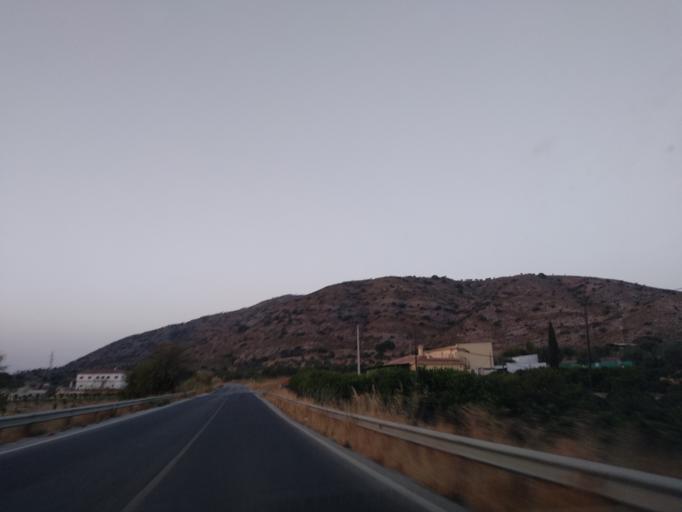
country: ES
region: Andalusia
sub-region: Provincia de Malaga
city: Cartama
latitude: 36.6876
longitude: -4.6522
